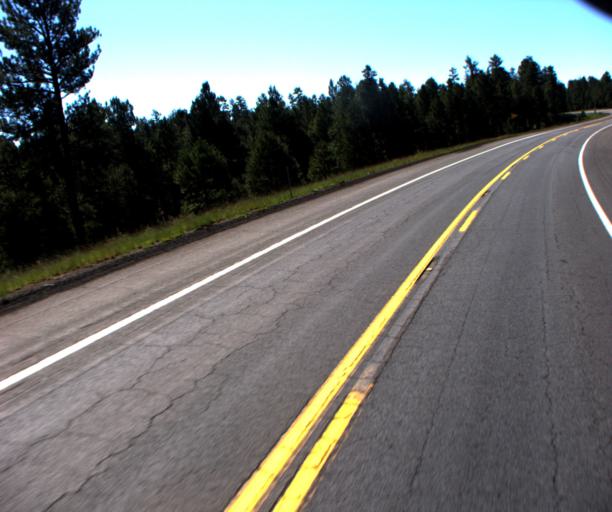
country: US
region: New Mexico
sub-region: Catron County
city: Reserve
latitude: 33.8190
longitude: -109.0741
